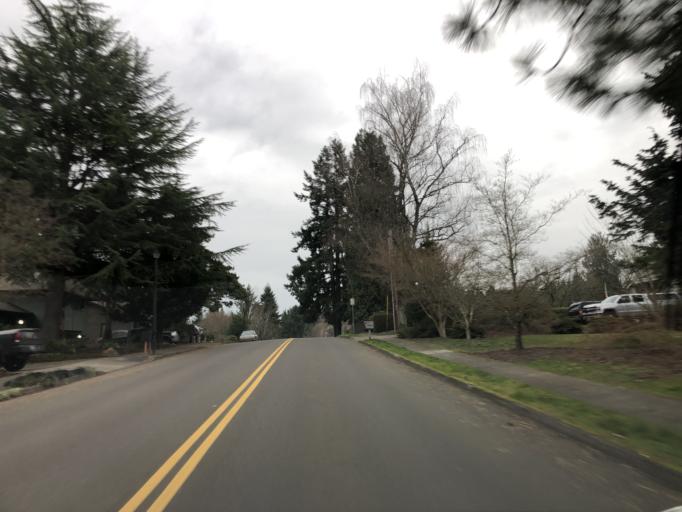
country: US
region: Oregon
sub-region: Washington County
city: King City
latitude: 45.4204
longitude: -122.7954
